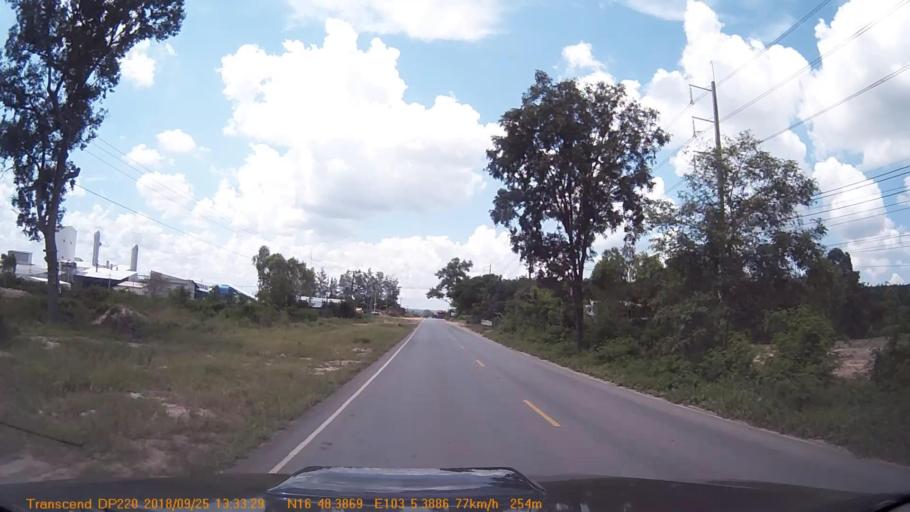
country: TH
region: Khon Kaen
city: Kranuan
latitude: 16.8065
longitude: 103.0898
